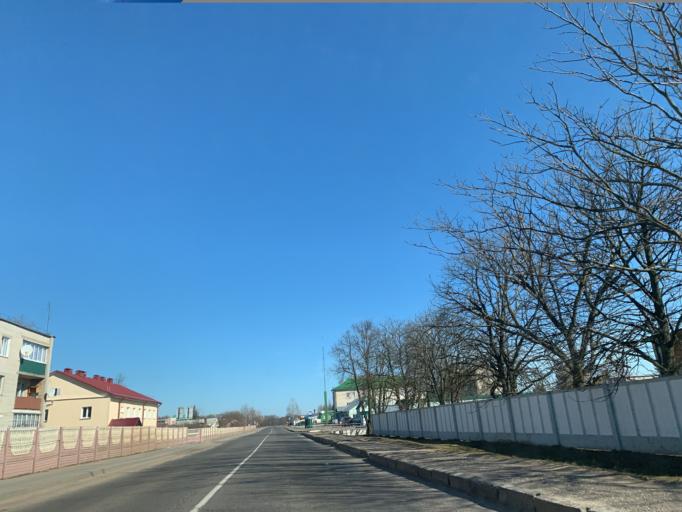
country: BY
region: Minsk
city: Nyasvizh
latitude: 53.2135
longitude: 26.6983
